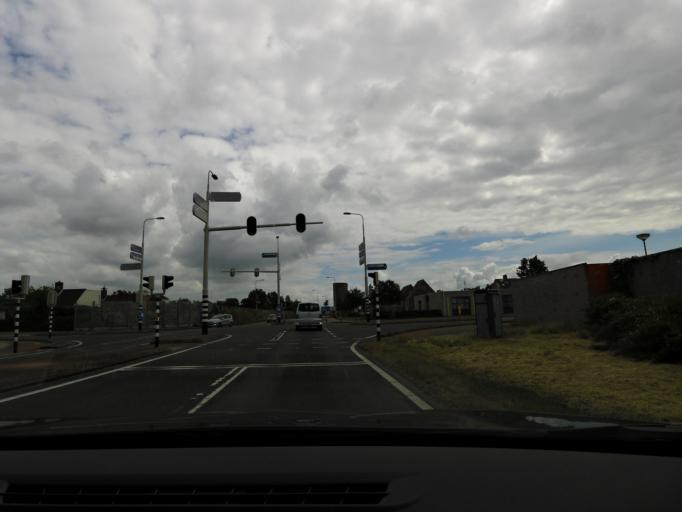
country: NL
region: Zeeland
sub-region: Gemeente Vlissingen
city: Vlissingen
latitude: 51.4628
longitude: 3.5678
